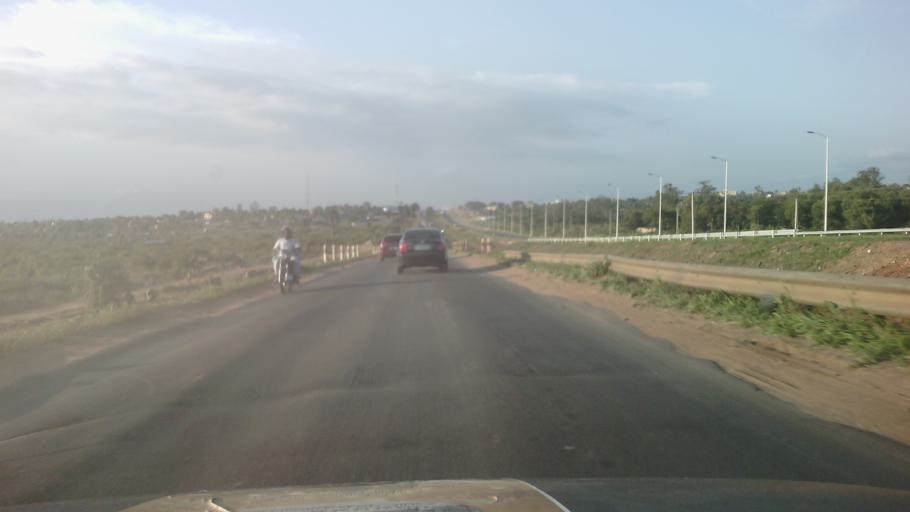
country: TG
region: Maritime
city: Tsevie
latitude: 6.3069
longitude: 1.2153
